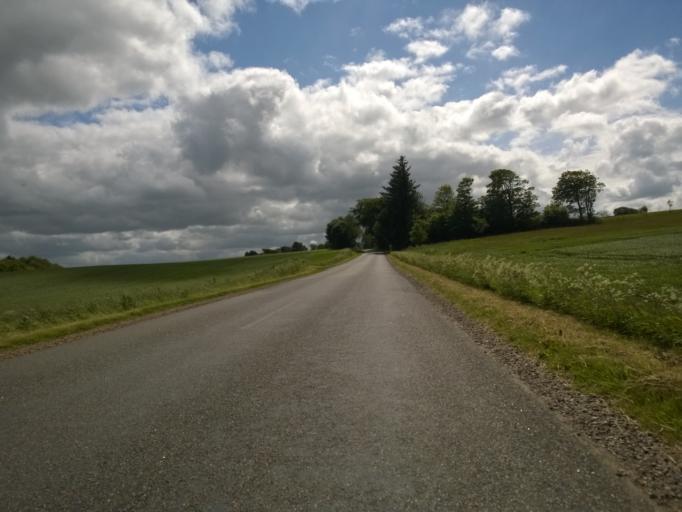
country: DK
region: Central Jutland
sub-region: Holstebro Kommune
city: Vinderup
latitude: 56.4407
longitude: 8.8609
